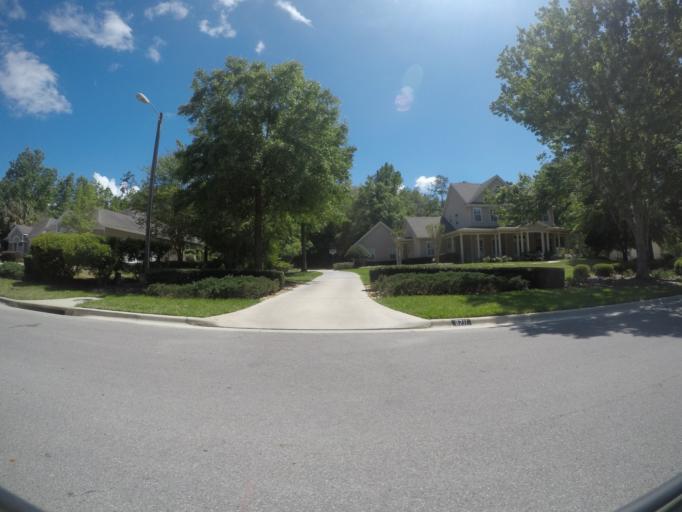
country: US
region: Florida
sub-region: Alachua County
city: Gainesville
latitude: 29.6167
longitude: -82.4347
